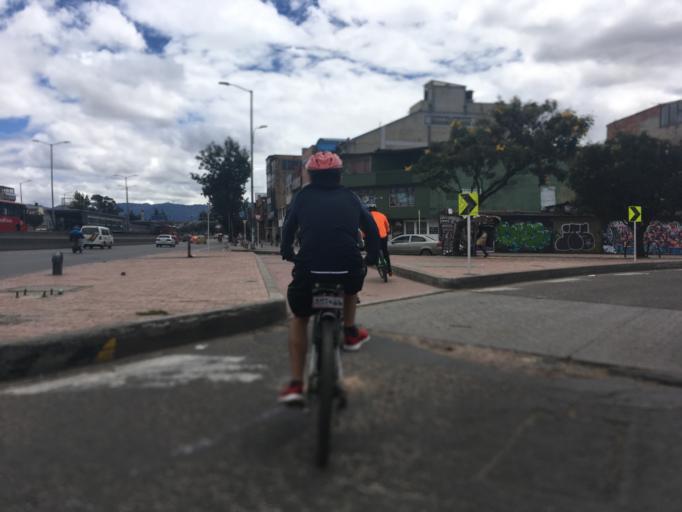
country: CO
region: Bogota D.C.
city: Bogota
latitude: 4.5952
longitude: -74.1440
